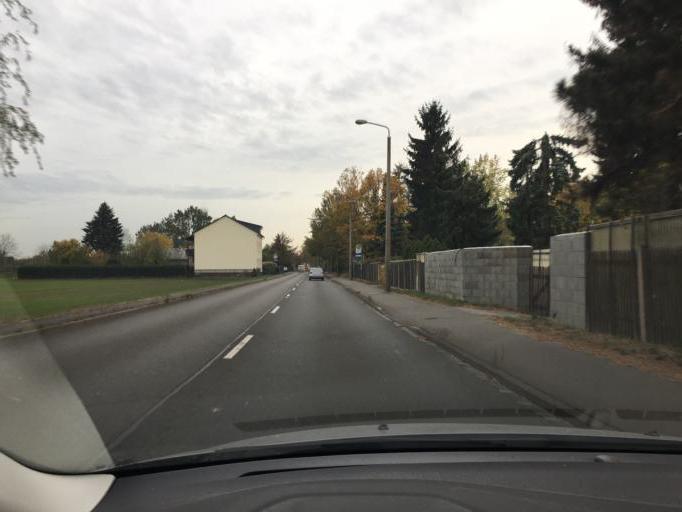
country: DE
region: Saxony
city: Taucha
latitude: 51.3378
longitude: 12.4439
